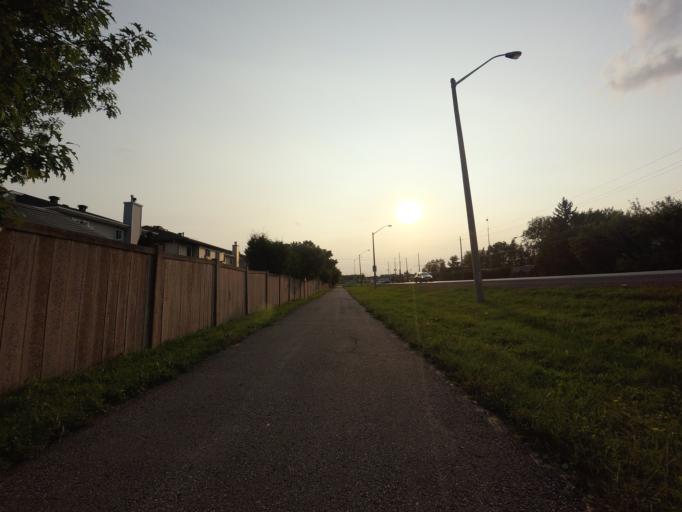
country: CA
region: Ontario
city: Bells Corners
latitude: 45.2755
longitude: -75.7754
